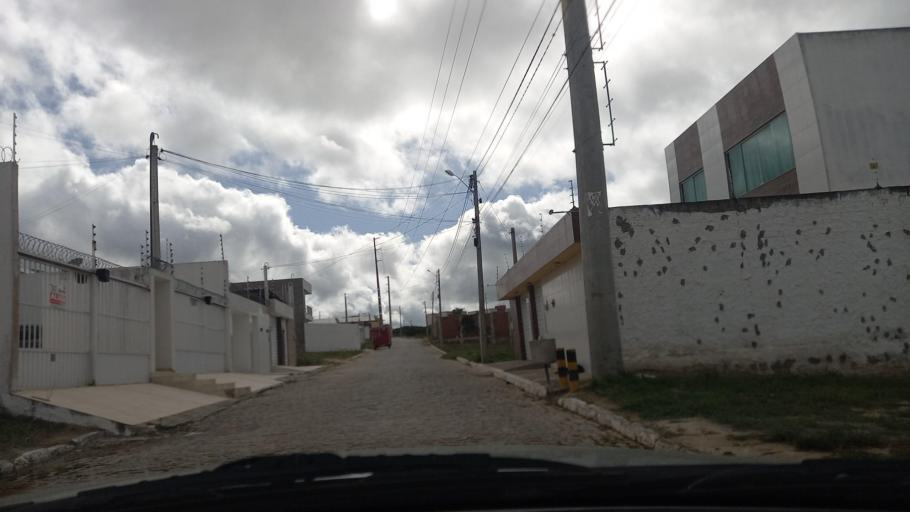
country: BR
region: Pernambuco
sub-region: Caruaru
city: Caruaru
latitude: -8.3056
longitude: -35.9550
